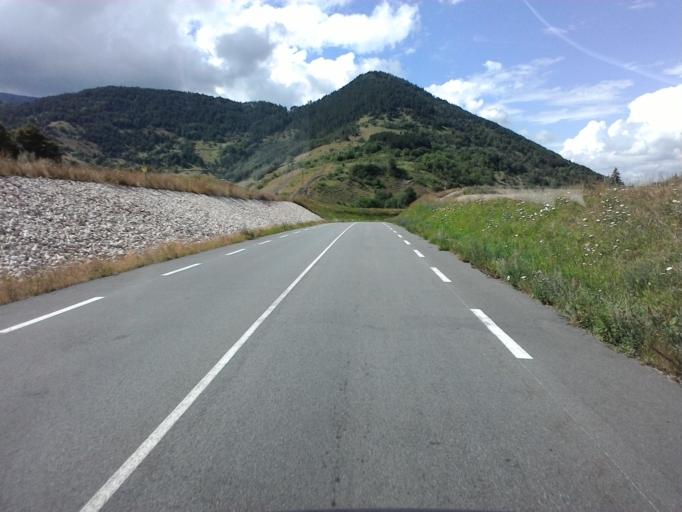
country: FR
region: Rhone-Alpes
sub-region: Departement de l'Isere
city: La Mure
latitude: 44.8975
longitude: 5.7823
